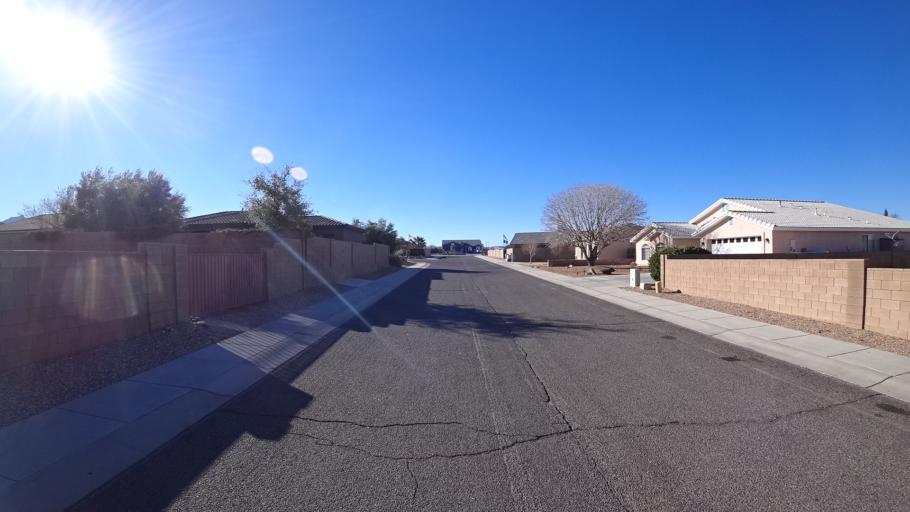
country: US
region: Arizona
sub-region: Mohave County
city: Kingman
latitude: 35.1854
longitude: -113.9998
